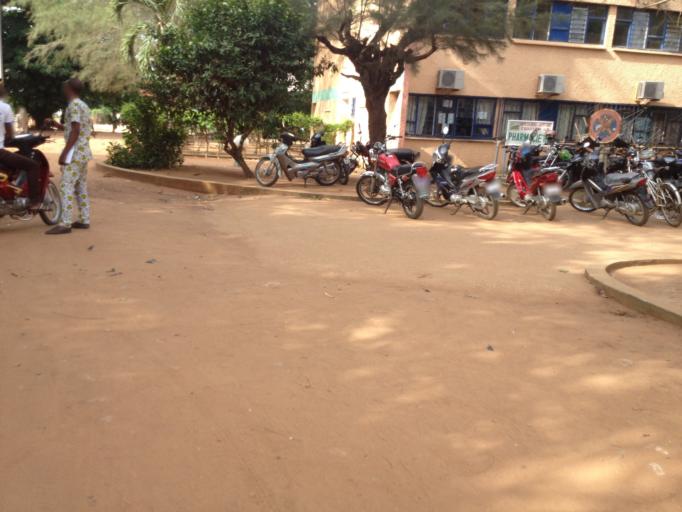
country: BJ
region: Atlantique
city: Abomey-Calavi
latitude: 6.4131
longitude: 2.3426
